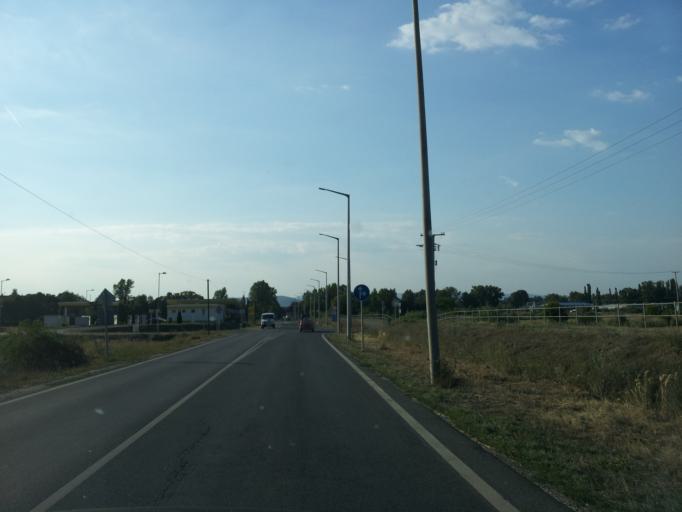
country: HU
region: Pest
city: Dunabogdany
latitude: 47.7860
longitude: 19.0450
